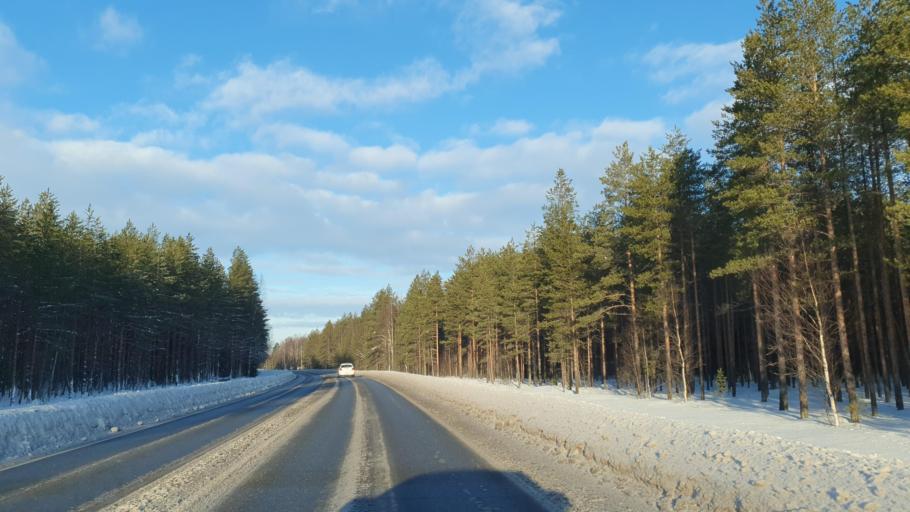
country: FI
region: Northern Ostrobothnia
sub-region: Oulunkaari
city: Utajaervi
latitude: 64.7762
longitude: 26.3022
